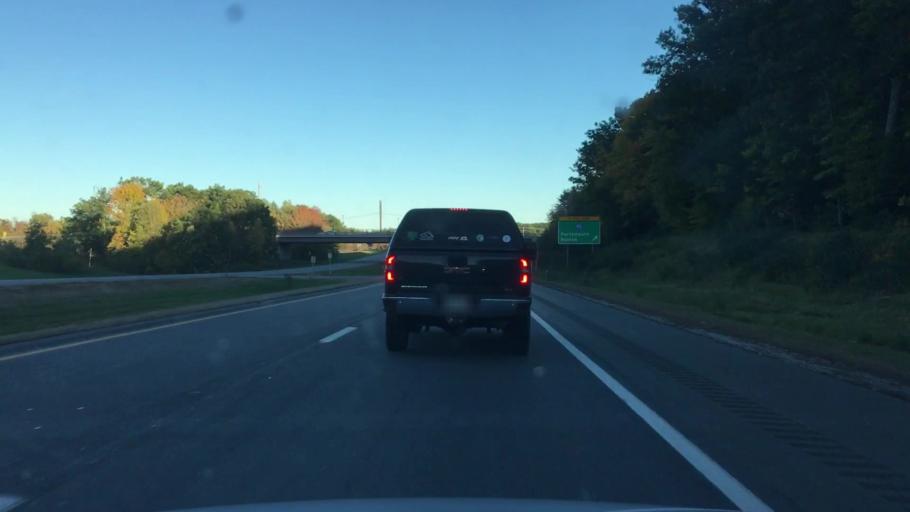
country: US
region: New Hampshire
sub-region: Rockingham County
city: Hampton
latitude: 42.9622
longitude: -70.8664
